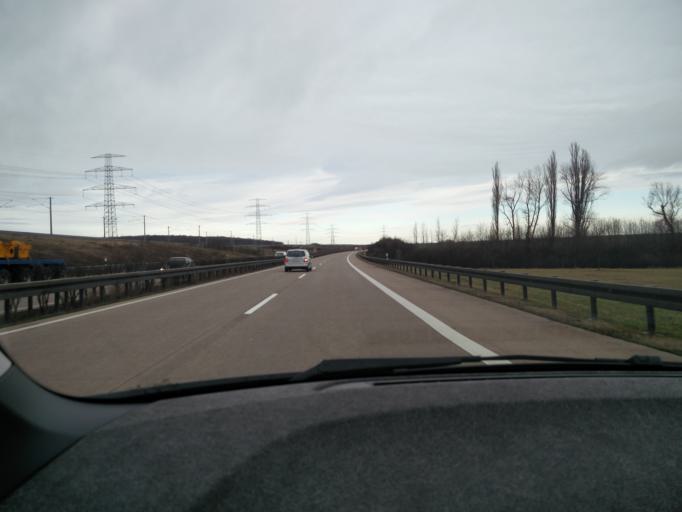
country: DE
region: Thuringia
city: Behringen
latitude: 50.7997
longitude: 10.9996
